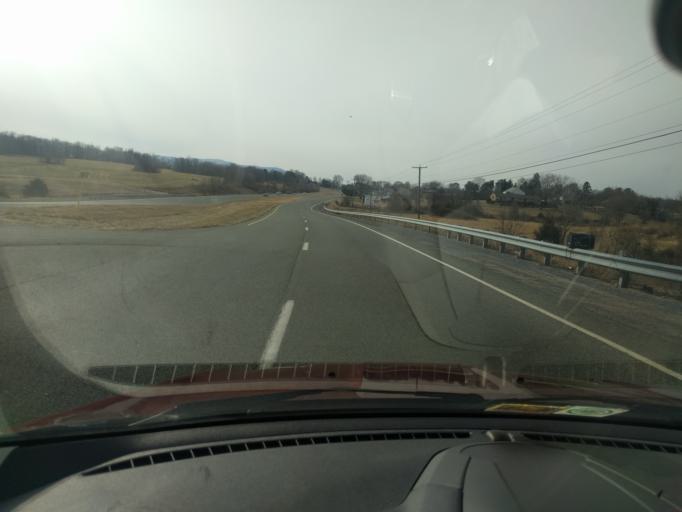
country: US
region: Virginia
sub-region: Augusta County
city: Lyndhurst
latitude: 38.0527
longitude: -78.9642
